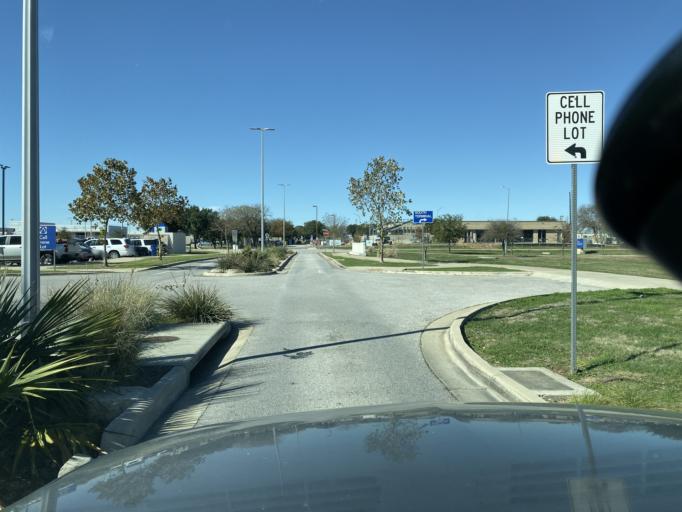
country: US
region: Texas
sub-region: Travis County
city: Hornsby Bend
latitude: 30.2113
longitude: -97.6665
